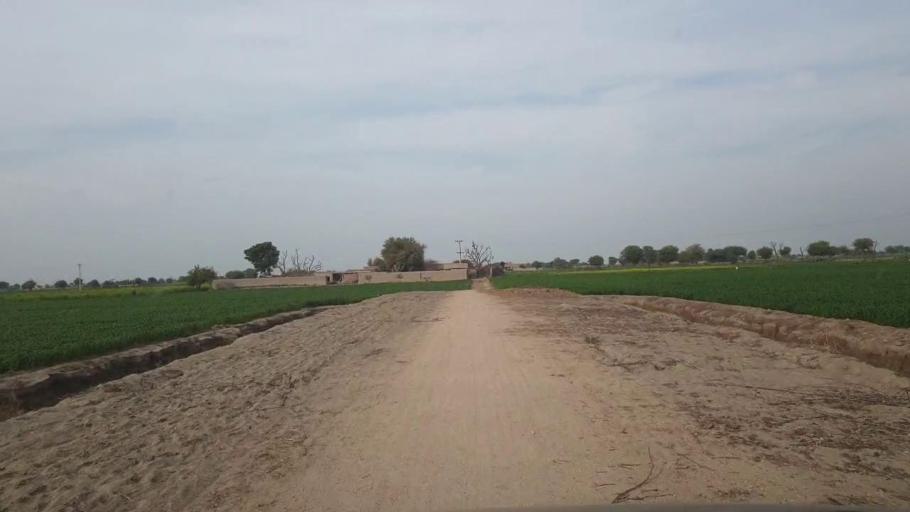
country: PK
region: Sindh
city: Shahpur Chakar
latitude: 26.1206
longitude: 68.5131
